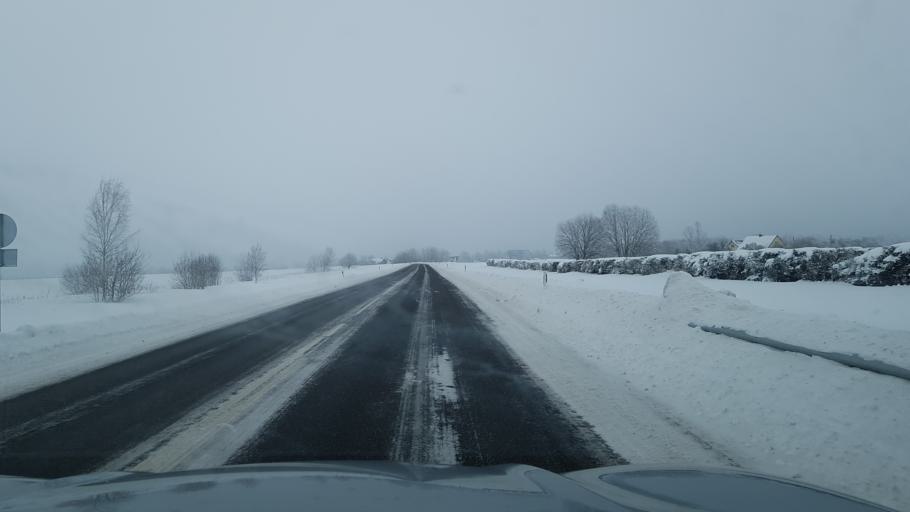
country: EE
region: Ida-Virumaa
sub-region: Johvi vald
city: Johvi
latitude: 59.3197
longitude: 27.3949
